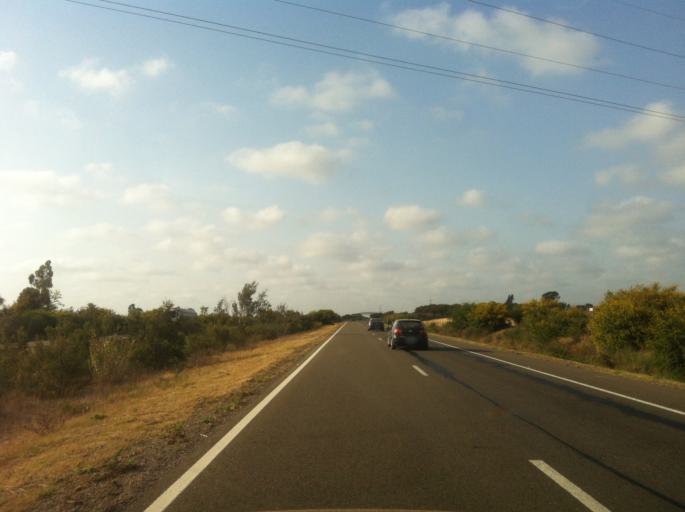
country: MA
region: Gharb-Chrarda-Beni Hssen
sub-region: Kenitra Province
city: Kenitra
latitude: 34.2298
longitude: -6.5638
